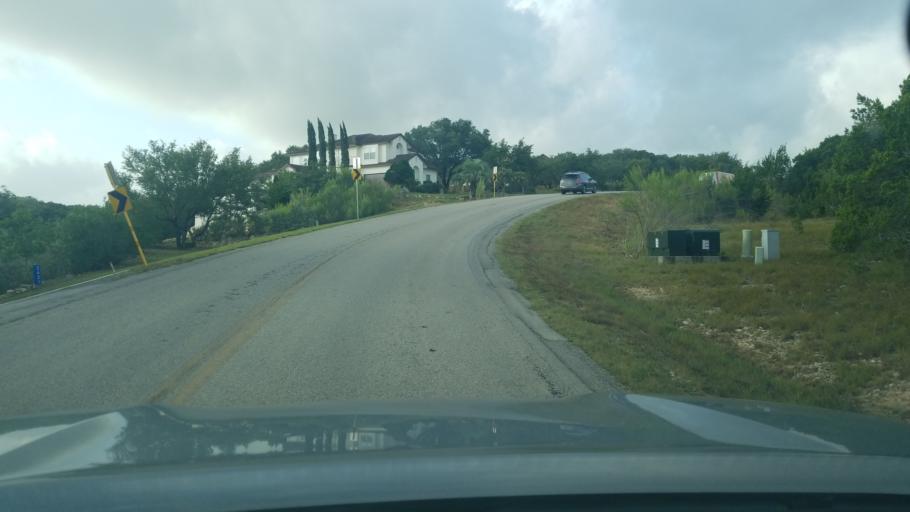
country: US
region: Texas
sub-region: Comal County
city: Bulverde
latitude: 29.8108
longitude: -98.4072
